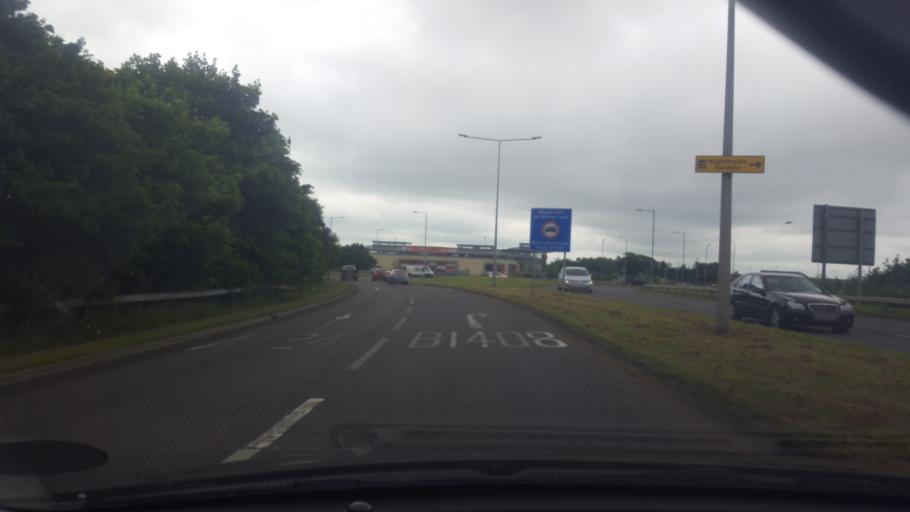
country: GB
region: England
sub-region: Essex
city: Eight Ash Green
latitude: 51.8893
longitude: 0.8282
